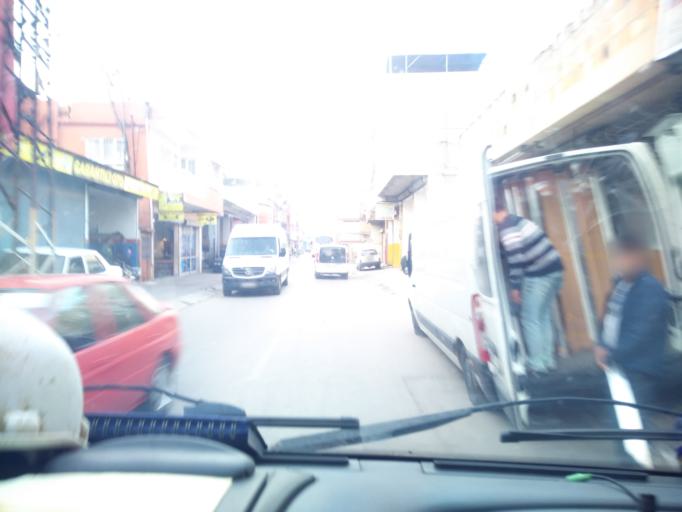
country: TR
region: Adana
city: Seyhan
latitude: 36.9979
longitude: 35.2798
